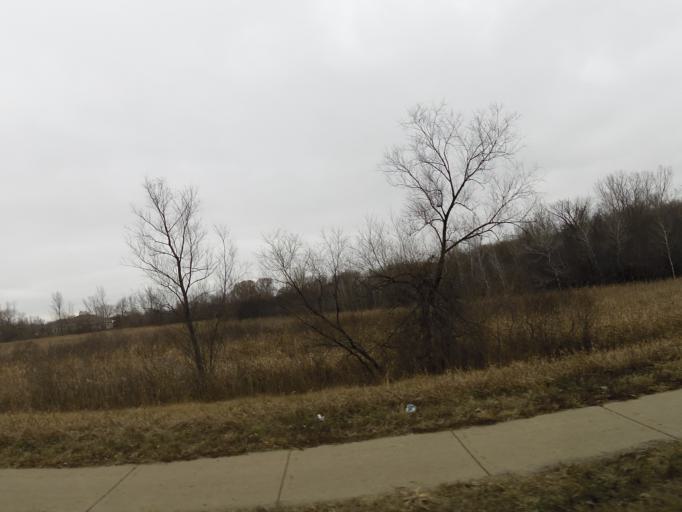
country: US
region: Minnesota
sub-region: Scott County
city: Savage
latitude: 44.7468
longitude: -93.3493
